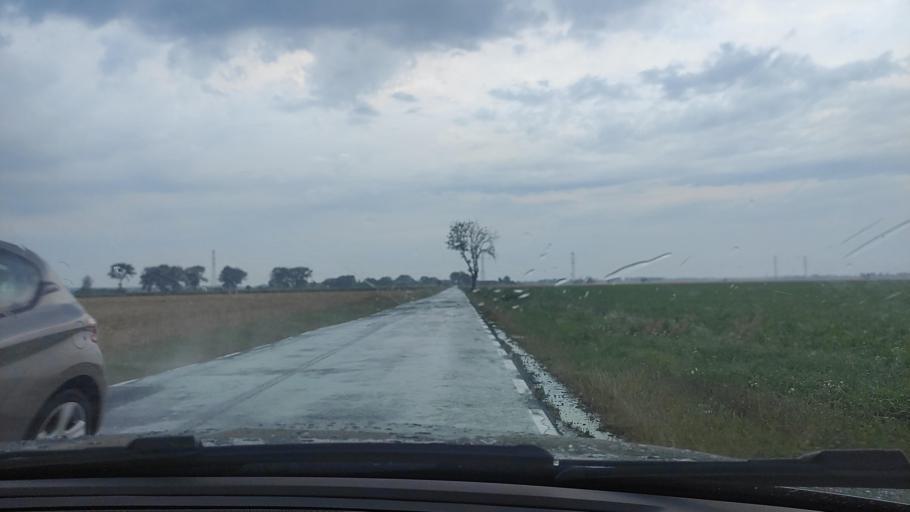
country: PL
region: Greater Poland Voivodeship
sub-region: Powiat poznanski
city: Kleszczewo
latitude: 52.2912
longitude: 17.1761
